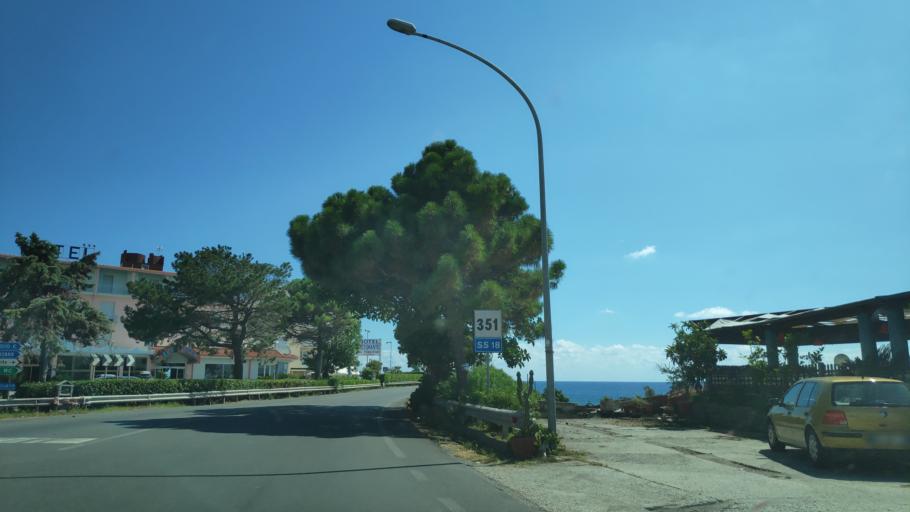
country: IT
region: Calabria
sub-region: Provincia di Cosenza
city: Campora San Giovanni
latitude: 39.0674
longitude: 16.0924
